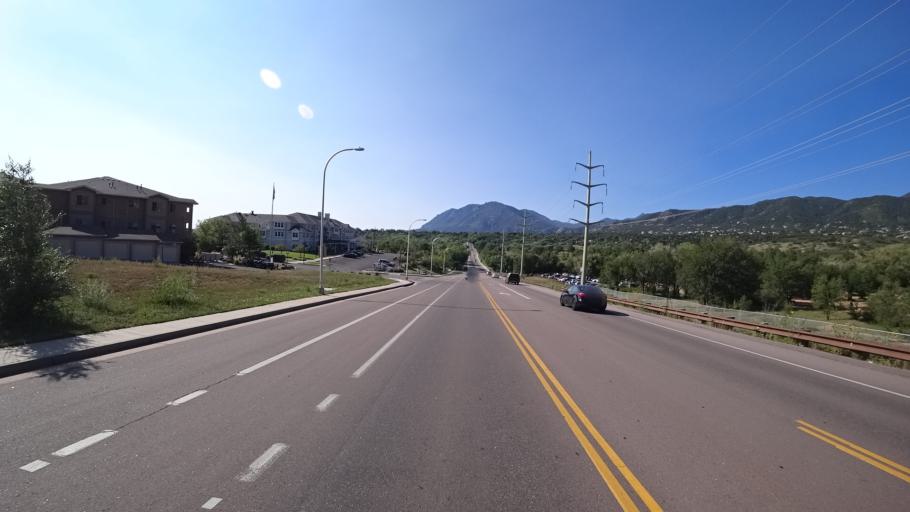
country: US
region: Colorado
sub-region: El Paso County
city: Colorado Springs
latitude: 38.8264
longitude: -104.8591
